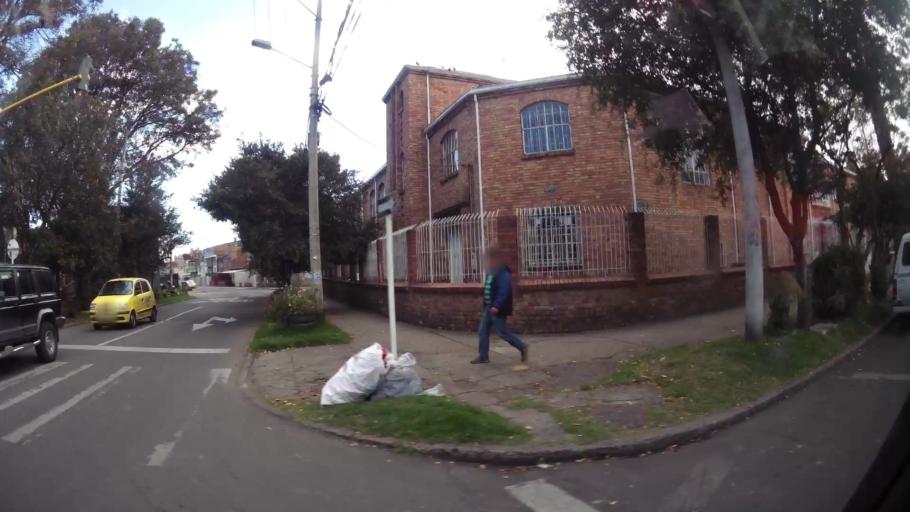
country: CO
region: Bogota D.C.
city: Bogota
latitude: 4.6545
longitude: -74.0692
